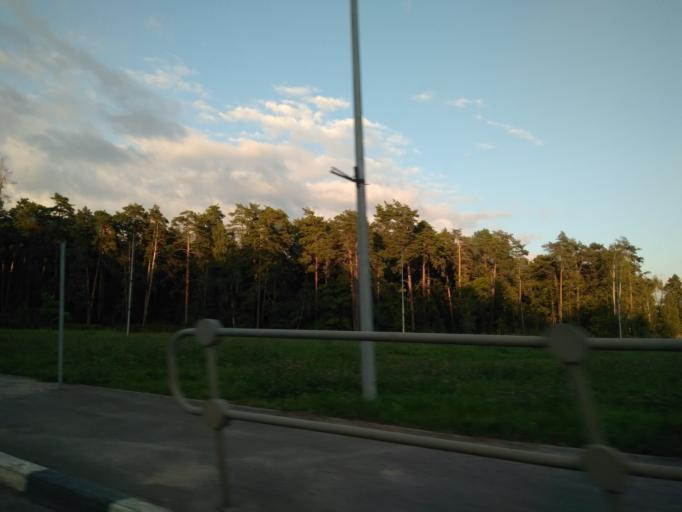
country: RU
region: Moskovskaya
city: Zhukovskiy
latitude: 55.5811
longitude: 38.1248
